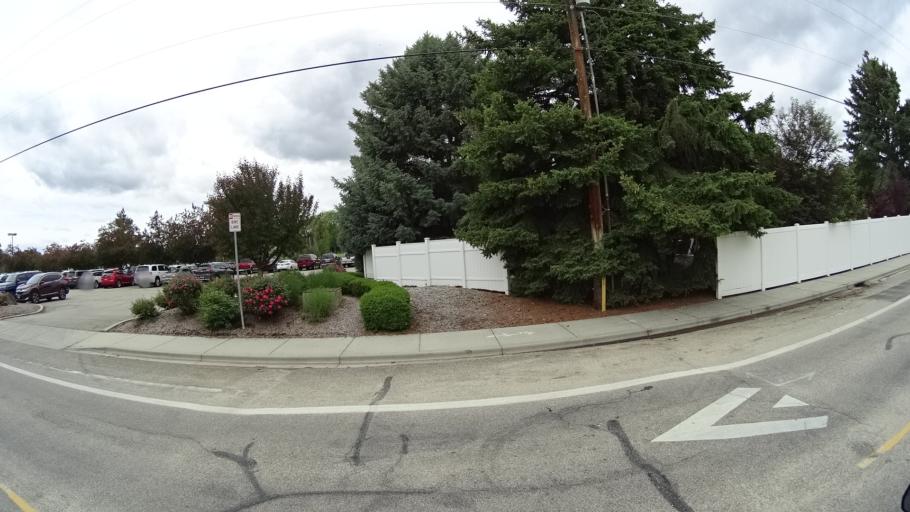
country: US
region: Idaho
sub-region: Ada County
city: Eagle
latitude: 43.7018
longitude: -116.3341
